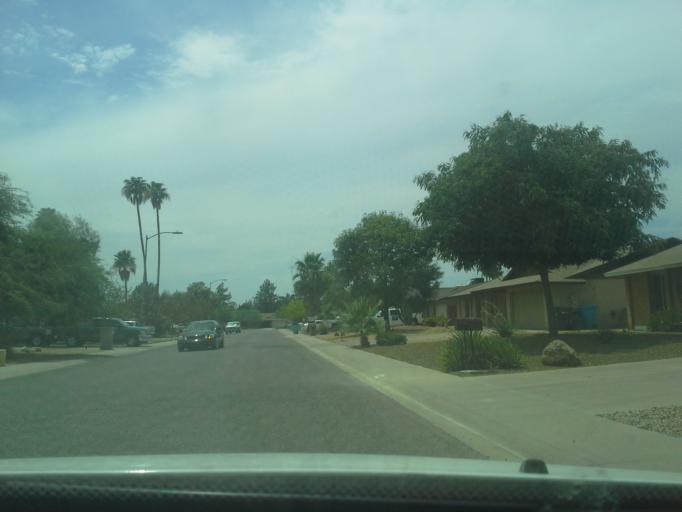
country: US
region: Arizona
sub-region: Maricopa County
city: Paradise Valley
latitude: 33.6111
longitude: -111.9838
